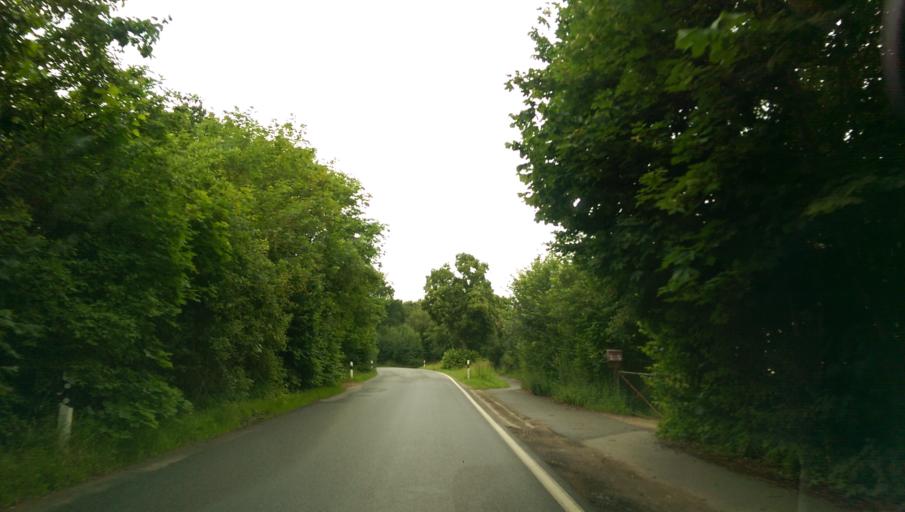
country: DE
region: Schleswig-Holstein
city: Ratekau
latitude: 53.9881
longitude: 10.6942
